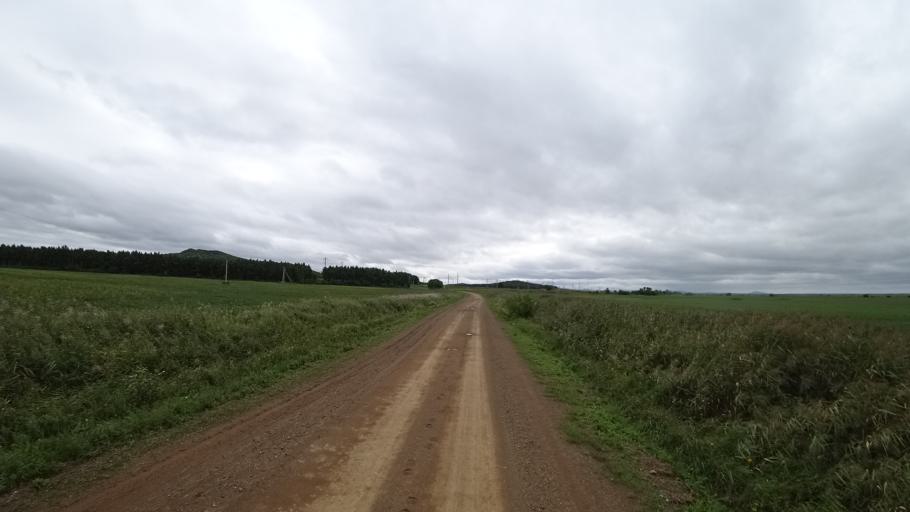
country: RU
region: Primorskiy
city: Chernigovka
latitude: 44.4827
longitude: 132.5744
